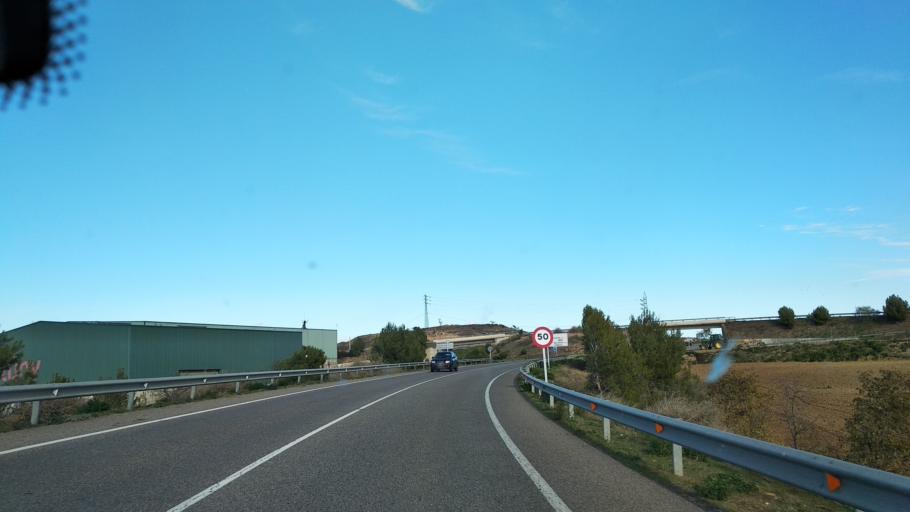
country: ES
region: Catalonia
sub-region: Provincia de Lleida
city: Balaguer
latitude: 41.7841
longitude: 0.7903
